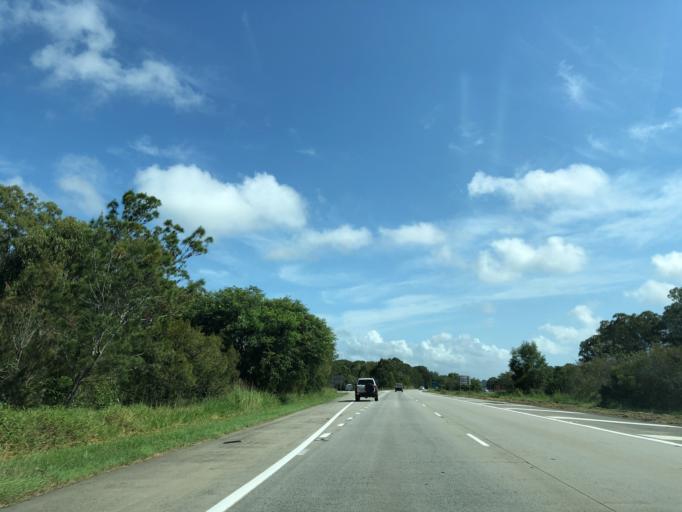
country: AU
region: New South Wales
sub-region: Byron Shire
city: Brunswick Heads
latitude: -28.6004
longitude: 153.5451
